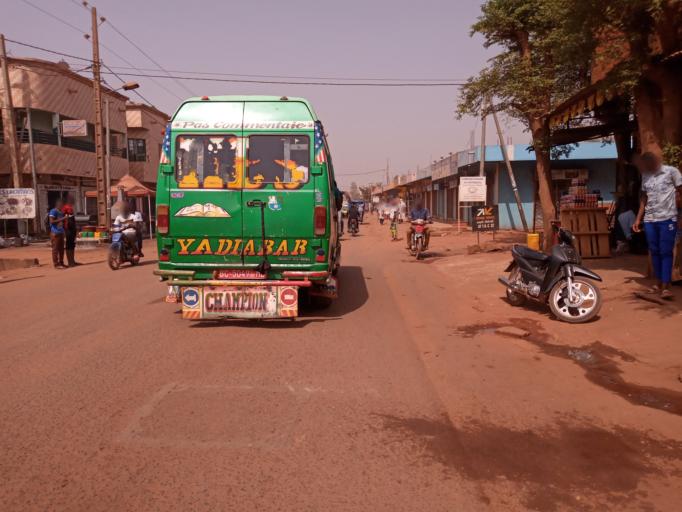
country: ML
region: Bamako
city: Bamako
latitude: 12.5883
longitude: -7.9716
